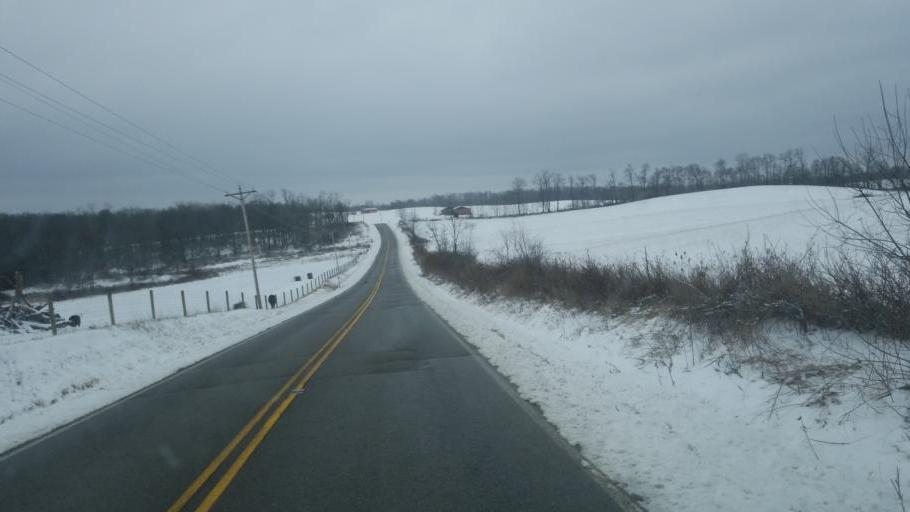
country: US
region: Ohio
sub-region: Knox County
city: Oak Hill
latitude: 40.4366
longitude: -82.1428
